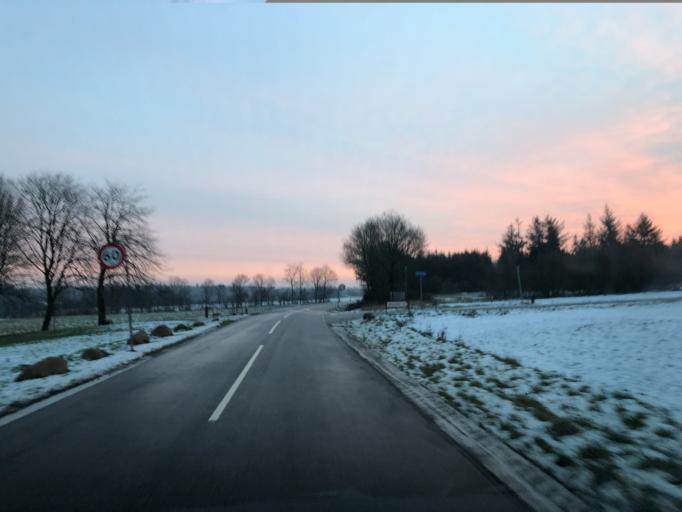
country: DK
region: Central Jutland
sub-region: Holstebro Kommune
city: Ulfborg
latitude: 56.2012
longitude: 8.4231
